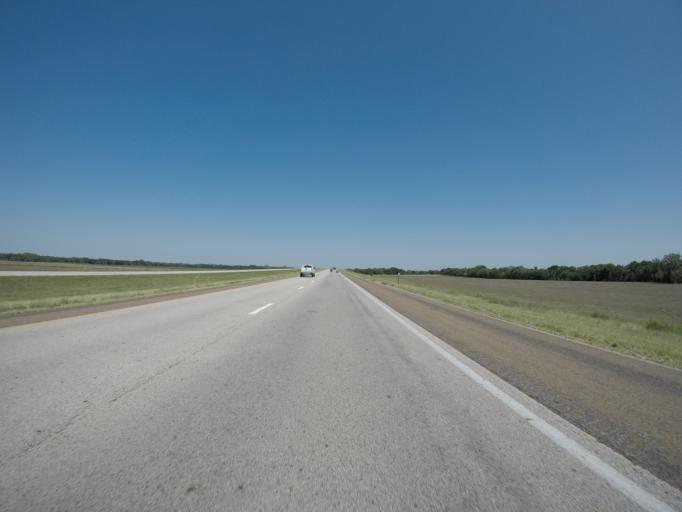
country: US
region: Kansas
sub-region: Saline County
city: Salina
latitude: 38.8782
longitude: -97.8133
